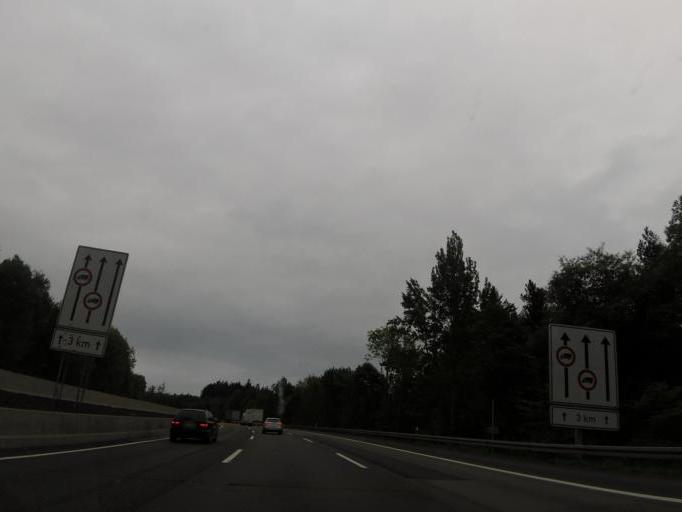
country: DE
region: Hesse
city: Schwarzenborn
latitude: 50.9609
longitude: 9.4858
